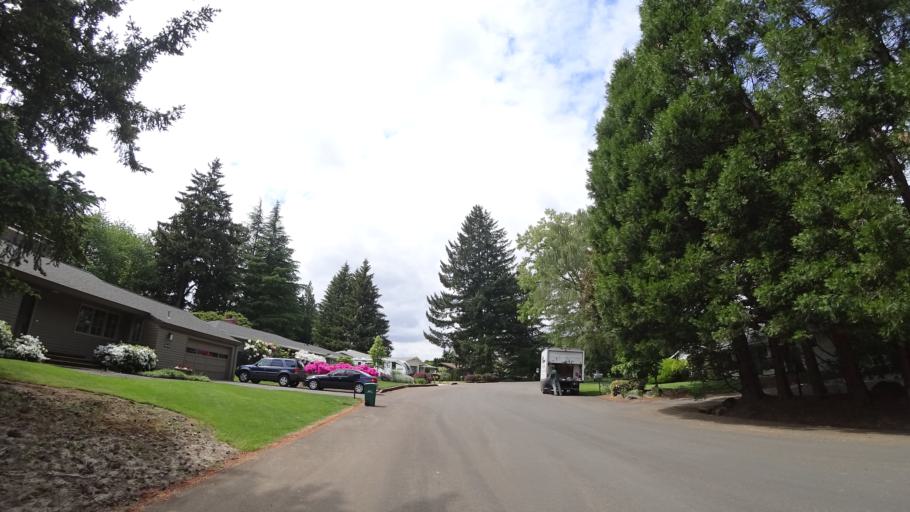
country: US
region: Oregon
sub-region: Washington County
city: Garden Home-Whitford
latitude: 45.4626
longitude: -122.7754
